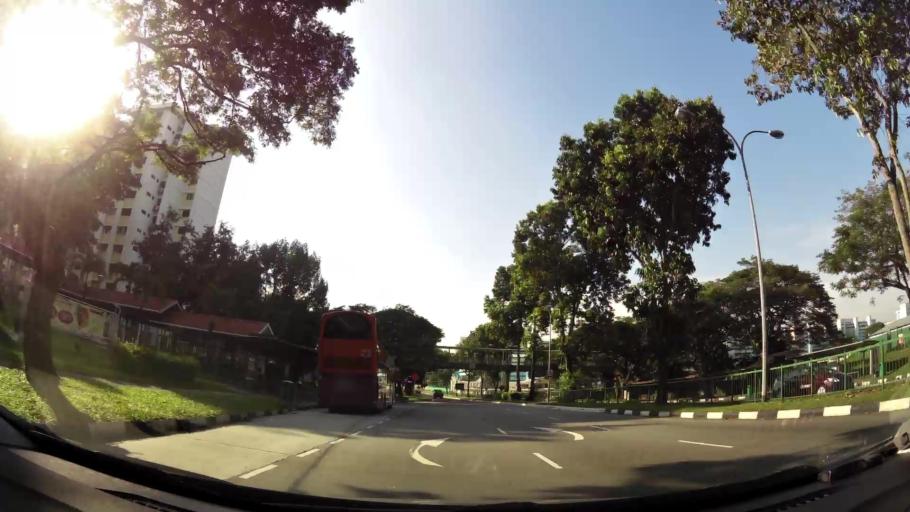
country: SG
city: Singapore
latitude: 1.3367
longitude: 103.9181
